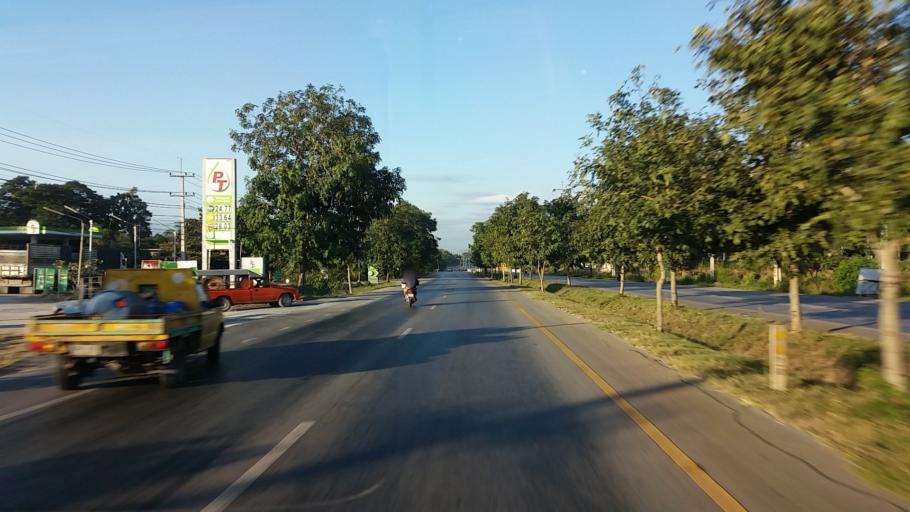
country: TH
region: Lop Buri
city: Chai Badan
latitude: 15.2095
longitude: 101.1142
